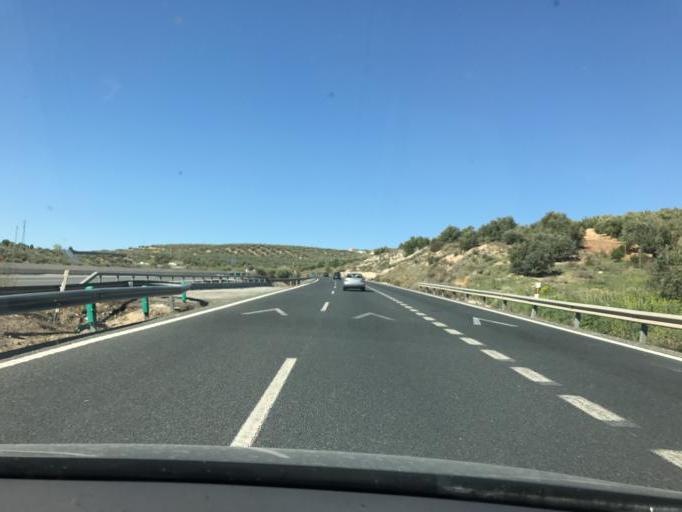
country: ES
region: Andalusia
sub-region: Provincia de Granada
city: Loja
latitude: 37.1565
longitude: -4.2208
